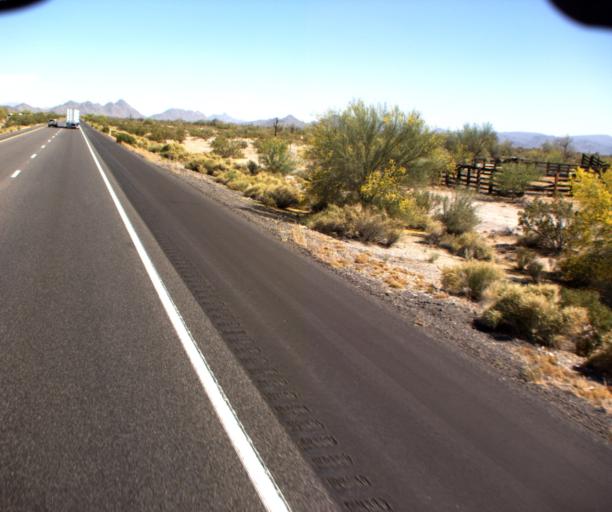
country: US
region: Arizona
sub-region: Maricopa County
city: Gila Bend
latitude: 32.9146
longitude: -112.6234
